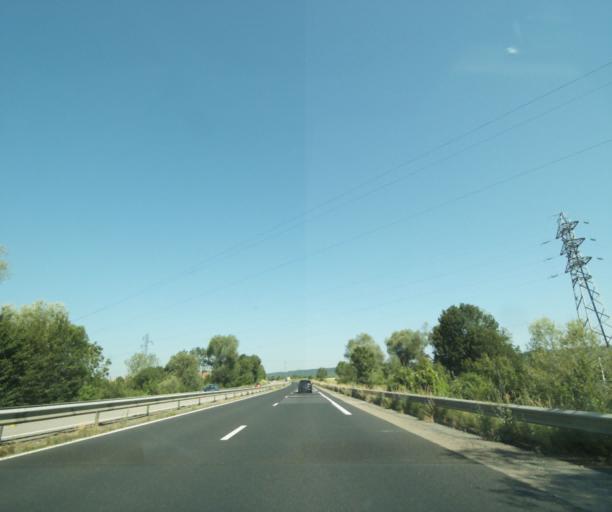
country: FR
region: Lorraine
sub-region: Departement de Meurthe-et-Moselle
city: Ecrouves
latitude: 48.6630
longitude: 5.8314
